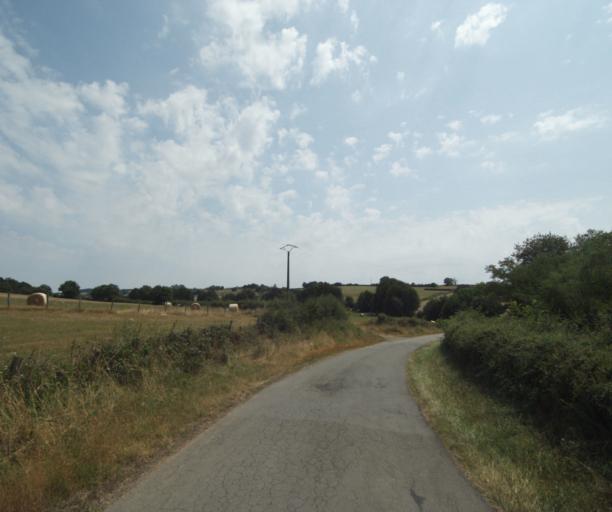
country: FR
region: Bourgogne
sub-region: Departement de Saone-et-Loire
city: Gueugnon
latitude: 46.5616
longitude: 4.0674
